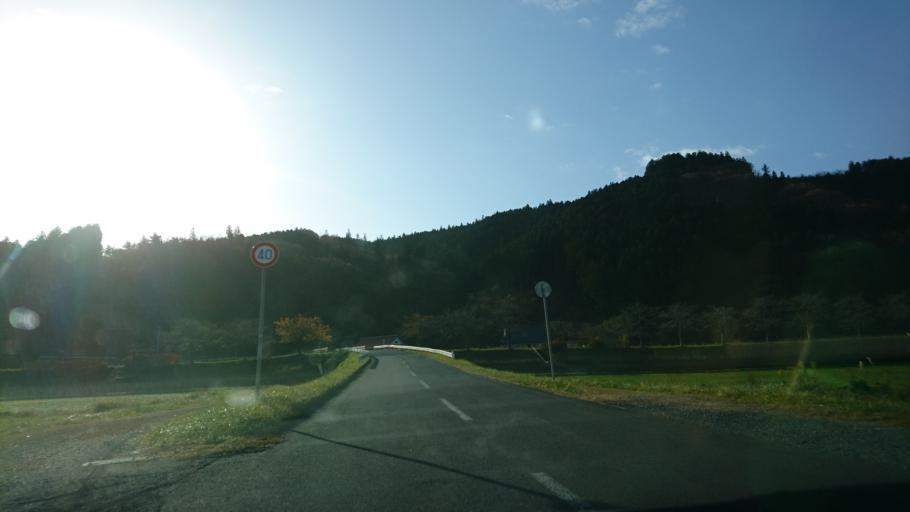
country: JP
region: Iwate
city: Ichinoseki
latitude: 38.8961
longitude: 141.2769
